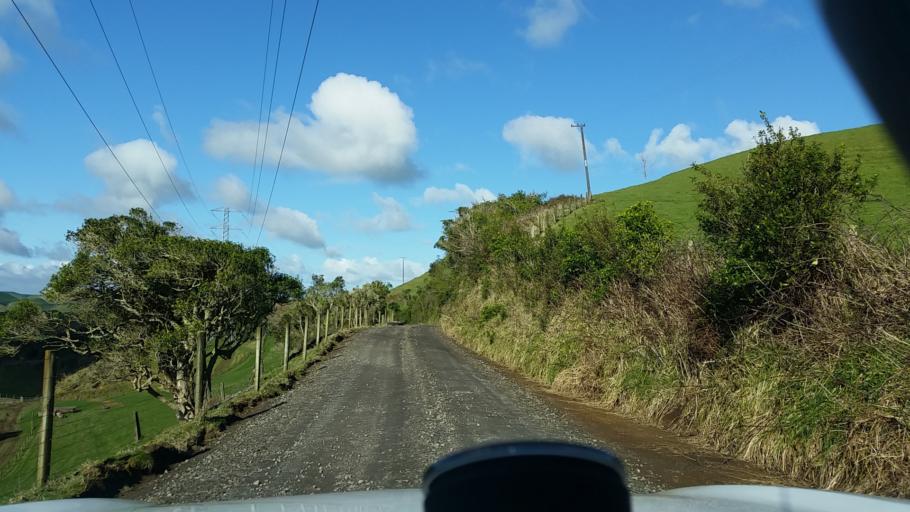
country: NZ
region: Taranaki
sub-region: South Taranaki District
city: Eltham
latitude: -39.4535
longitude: 174.3685
